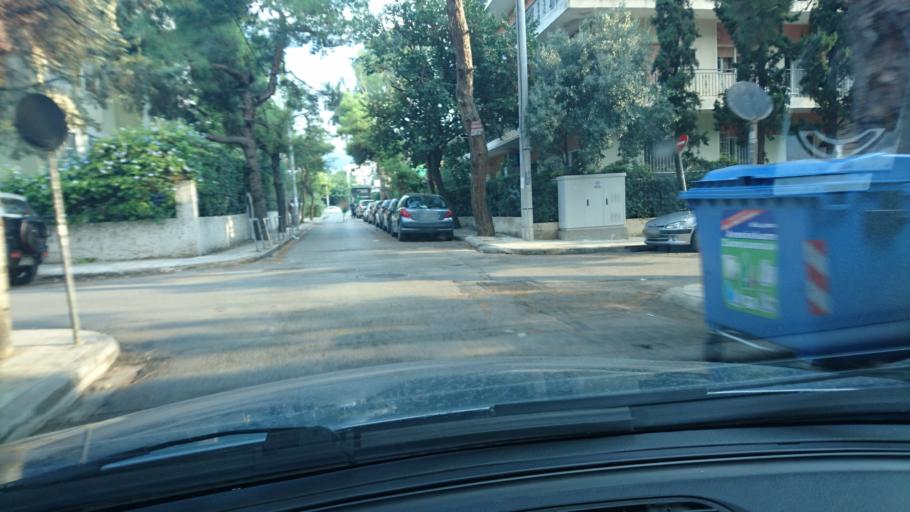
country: GR
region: Attica
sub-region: Nomarchia Athinas
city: Cholargos
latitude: 38.0072
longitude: 23.7976
